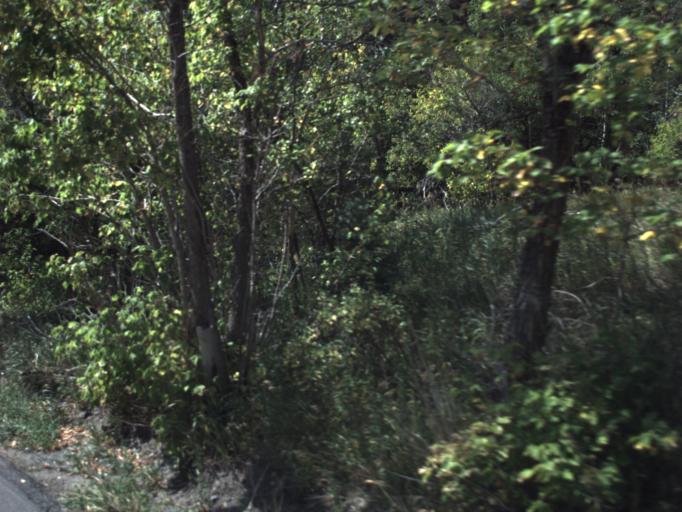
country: US
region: Utah
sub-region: Utah County
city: Highland
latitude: 40.4766
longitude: -111.6490
